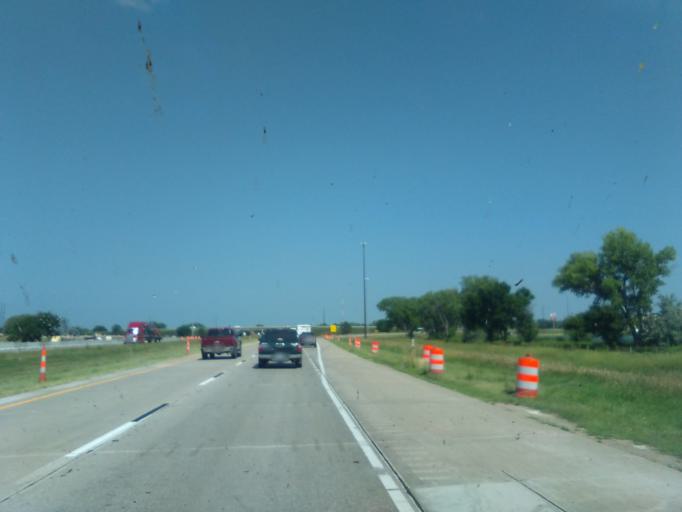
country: US
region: Nebraska
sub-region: Buffalo County
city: Kearney
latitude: 40.6694
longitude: -99.0925
